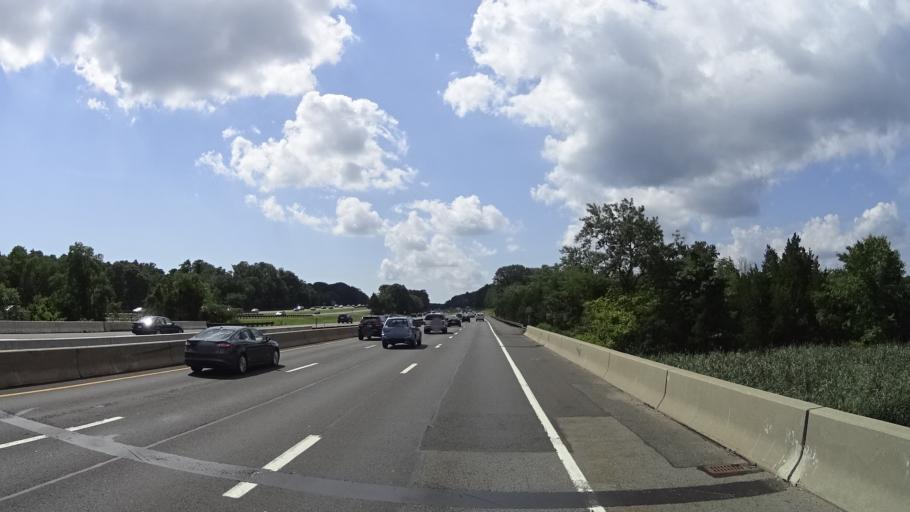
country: US
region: New Jersey
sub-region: Monmouth County
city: Tinton Falls
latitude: 40.3251
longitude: -74.0990
